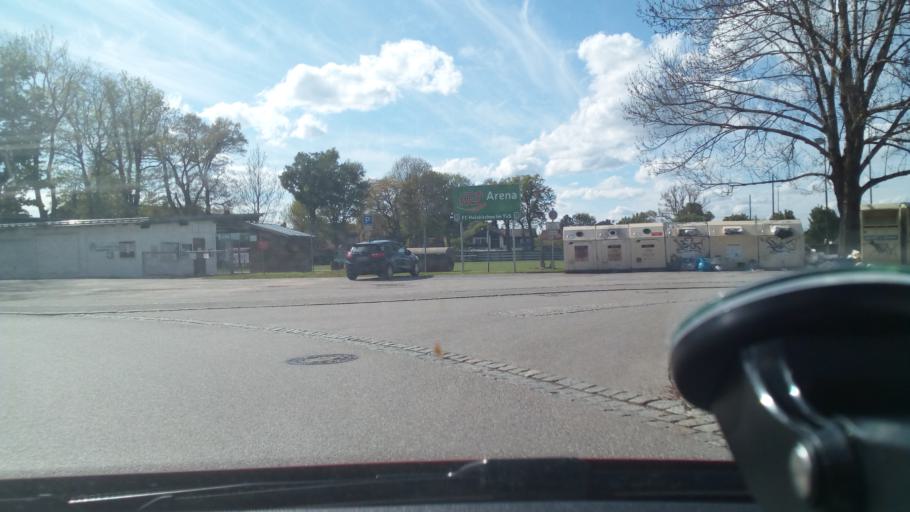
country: DE
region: Bavaria
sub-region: Upper Bavaria
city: Holzkirchen
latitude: 47.8792
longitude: 11.6924
